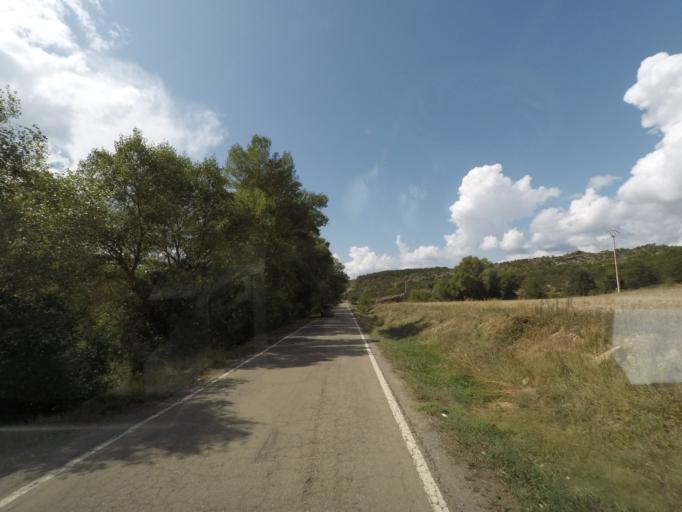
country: ES
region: Aragon
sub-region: Provincia de Huesca
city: Arguis
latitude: 42.4024
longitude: -0.3693
